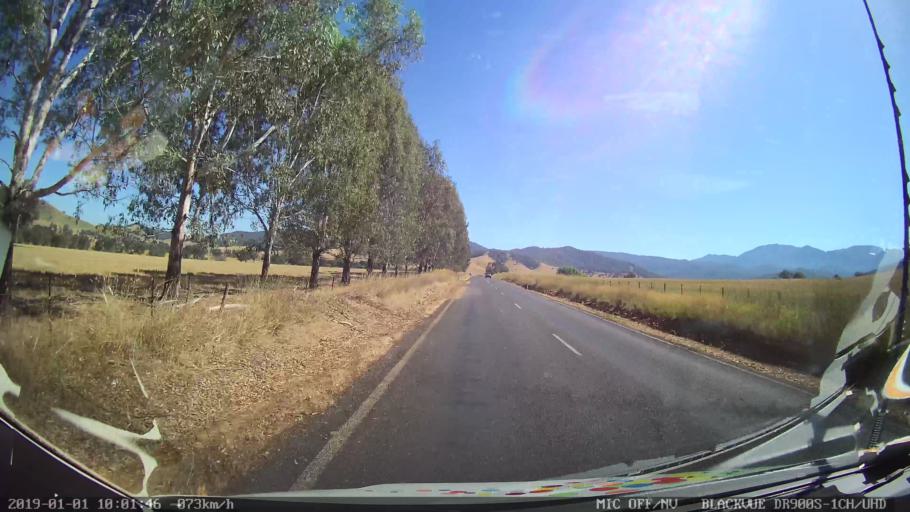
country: AU
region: New South Wales
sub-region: Snowy River
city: Jindabyne
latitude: -36.1881
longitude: 148.1008
